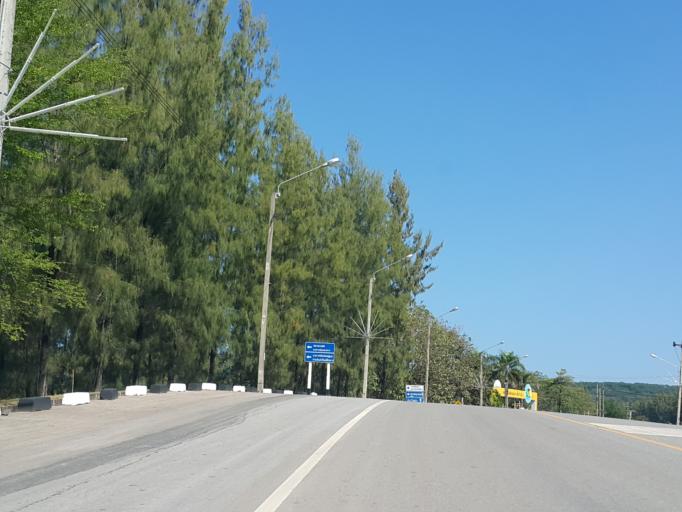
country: TH
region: Lampang
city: Mae Mo
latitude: 18.3152
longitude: 99.7447
